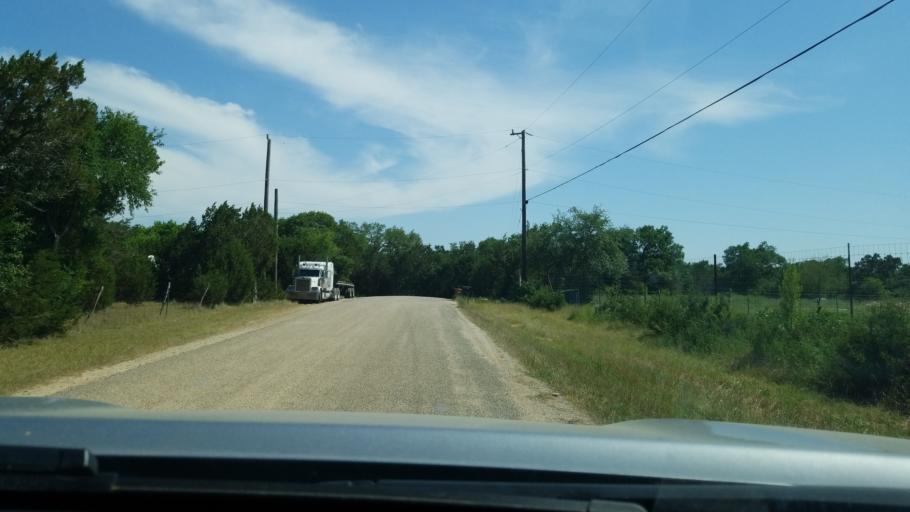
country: US
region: Texas
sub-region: Bexar County
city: Timberwood Park
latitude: 29.7461
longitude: -98.5179
